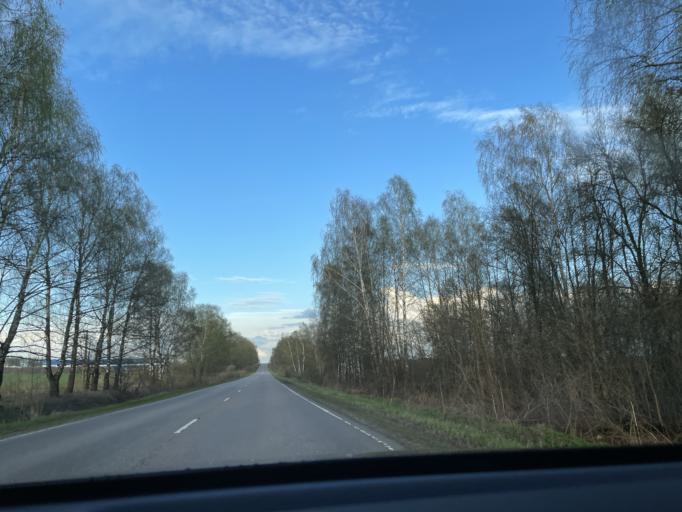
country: RU
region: Tula
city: Novogurovskiy
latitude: 54.5292
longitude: 37.3380
